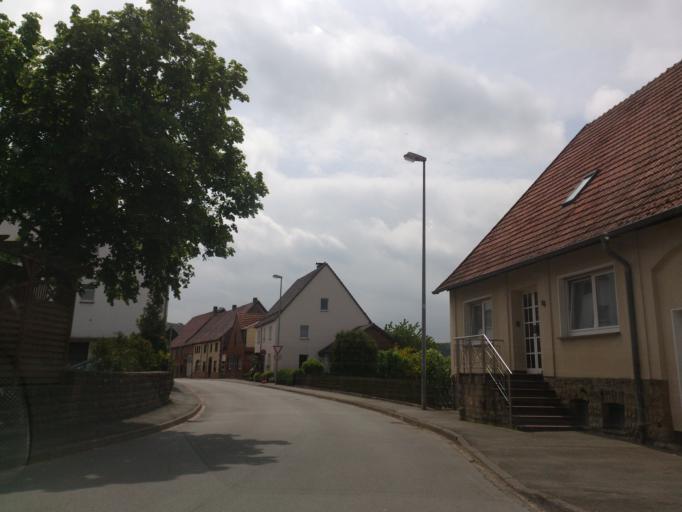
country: DE
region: North Rhine-Westphalia
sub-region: Regierungsbezirk Detmold
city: Willebadessen
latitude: 51.5603
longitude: 9.0513
